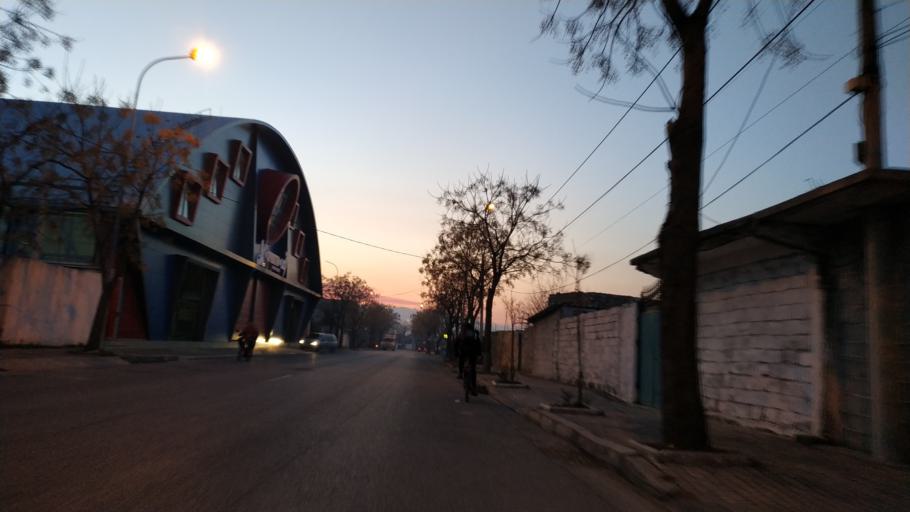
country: AL
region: Shkoder
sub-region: Rrethi i Shkodres
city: Shkoder
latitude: 42.0779
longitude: 19.5088
